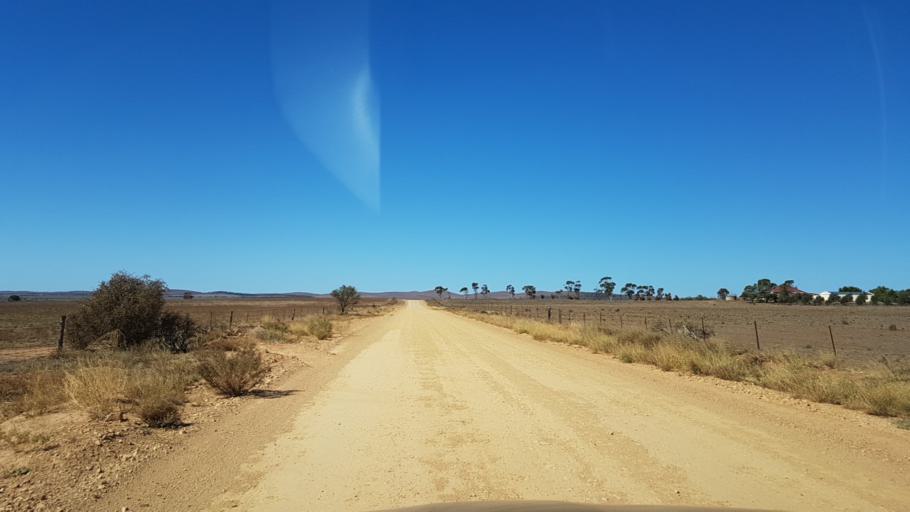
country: AU
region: South Australia
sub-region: Peterborough
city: Peterborough
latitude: -32.9911
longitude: 138.8408
